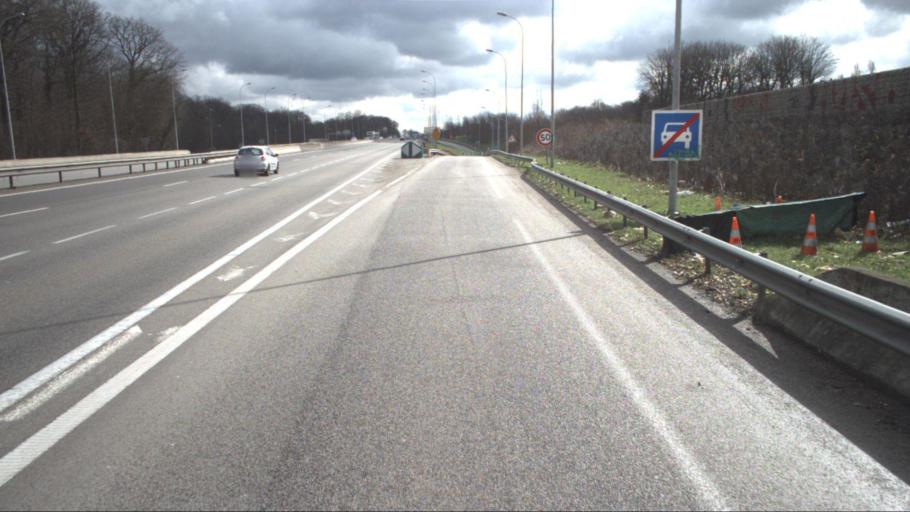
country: FR
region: Ile-de-France
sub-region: Departement des Yvelines
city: Buc
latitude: 48.7911
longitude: 2.1043
